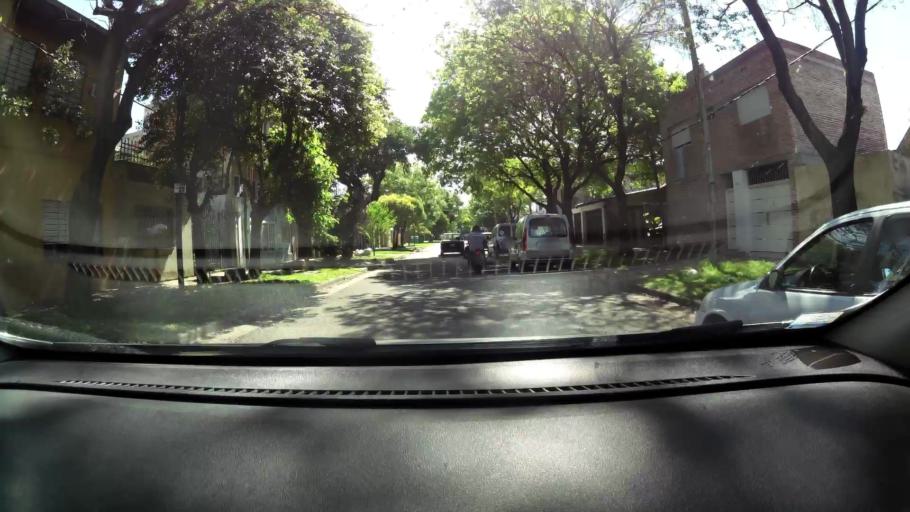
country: AR
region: Santa Fe
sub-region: Departamento de Rosario
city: Rosario
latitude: -32.9356
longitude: -60.7095
